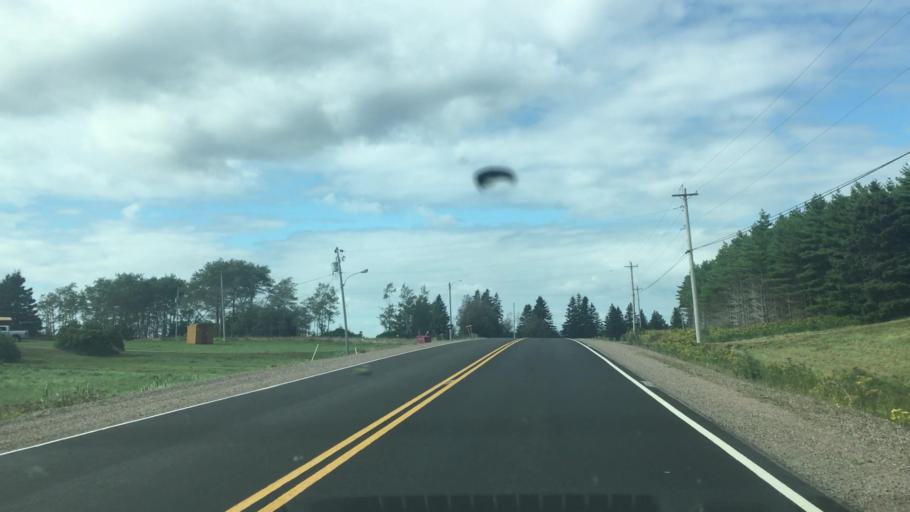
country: CA
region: Nova Scotia
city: Princeville
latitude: 45.7874
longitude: -60.7401
